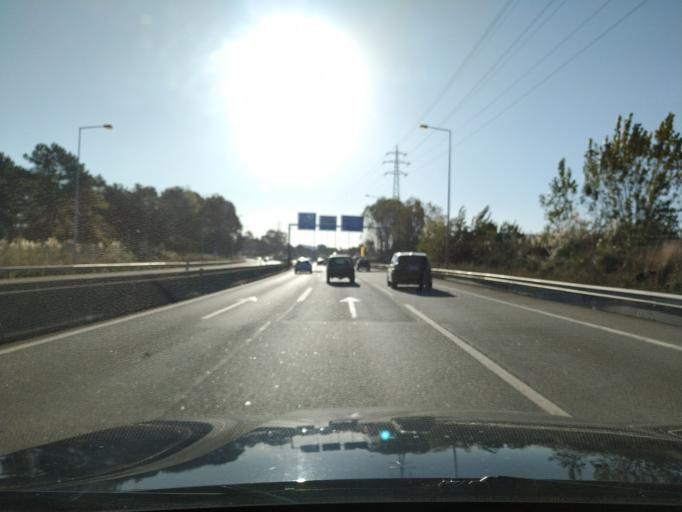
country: PT
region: Porto
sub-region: Vila Nova de Gaia
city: Canidelo
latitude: 41.1175
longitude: -8.6319
